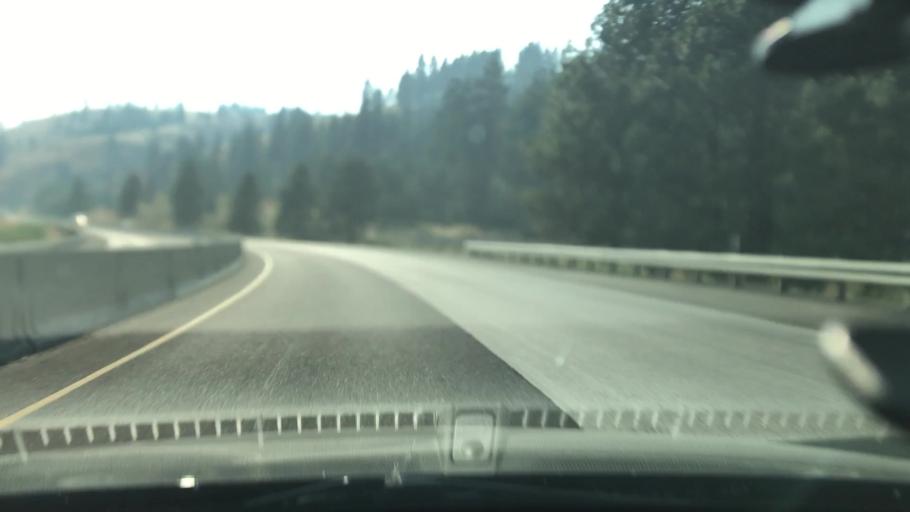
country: US
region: Oregon
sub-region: Union County
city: La Grande
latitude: 45.3548
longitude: -118.1883
